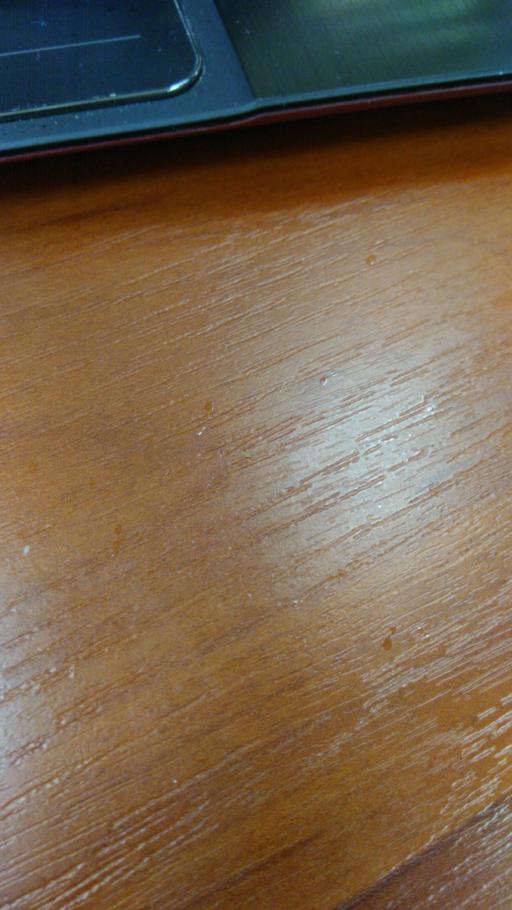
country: RU
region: Tverskaya
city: Emmaus
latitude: 56.7836
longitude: 36.0472
